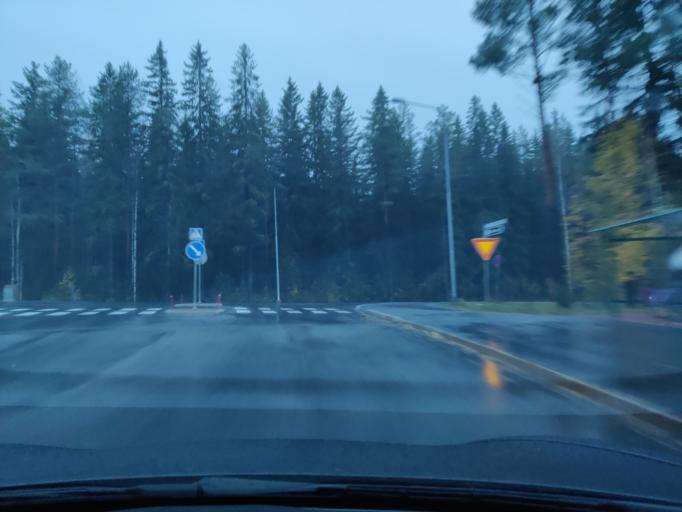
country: FI
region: Northern Savo
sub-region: Kuopio
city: Kuopio
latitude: 62.8327
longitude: 27.7129
